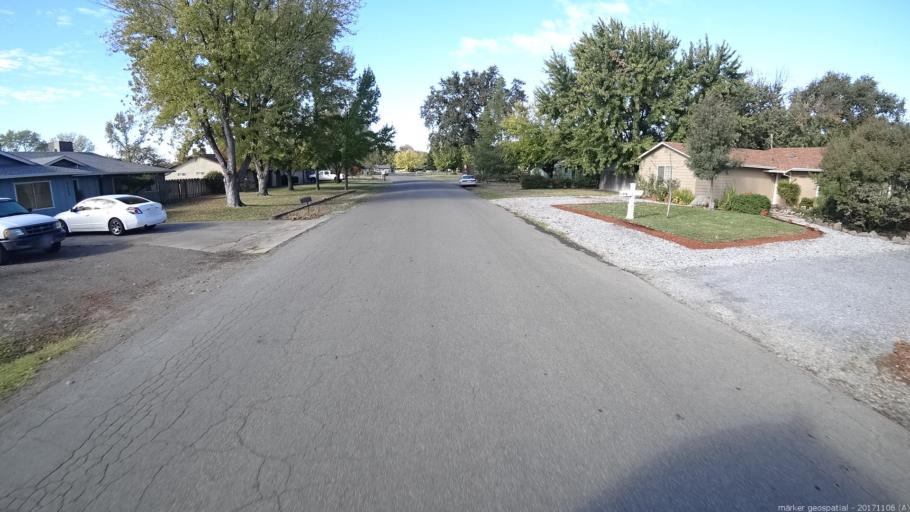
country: US
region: California
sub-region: Shasta County
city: Palo Cedro
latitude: 40.5404
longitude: -122.2401
